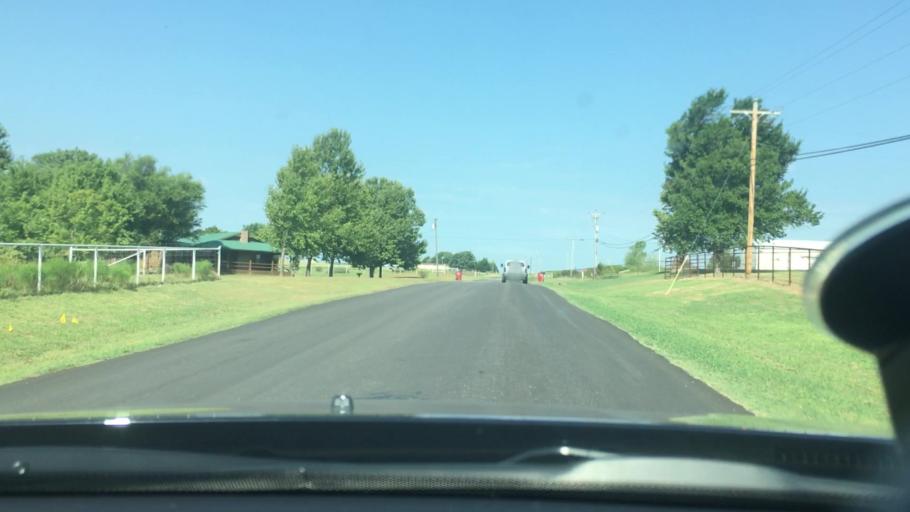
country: US
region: Oklahoma
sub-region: Garvin County
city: Lindsay
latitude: 34.7829
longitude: -97.6039
